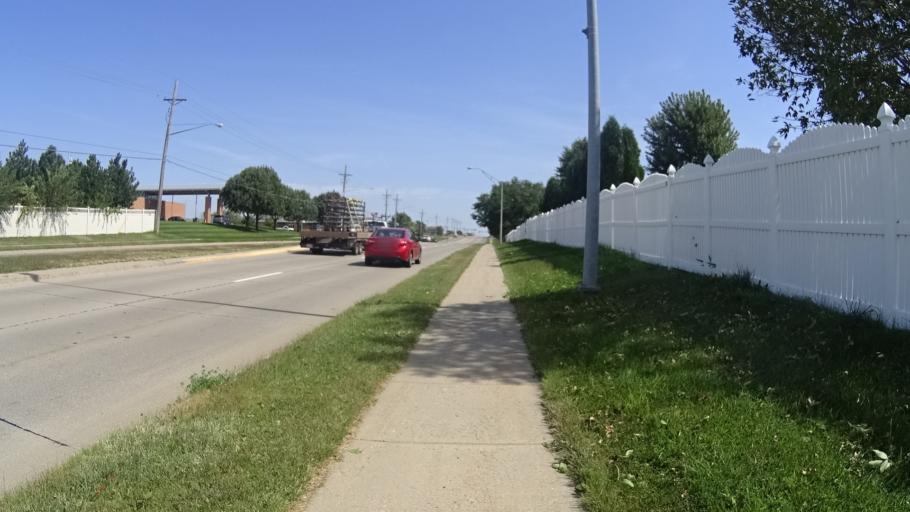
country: US
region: Nebraska
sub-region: Sarpy County
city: Papillion
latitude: 41.1761
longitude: -96.0685
